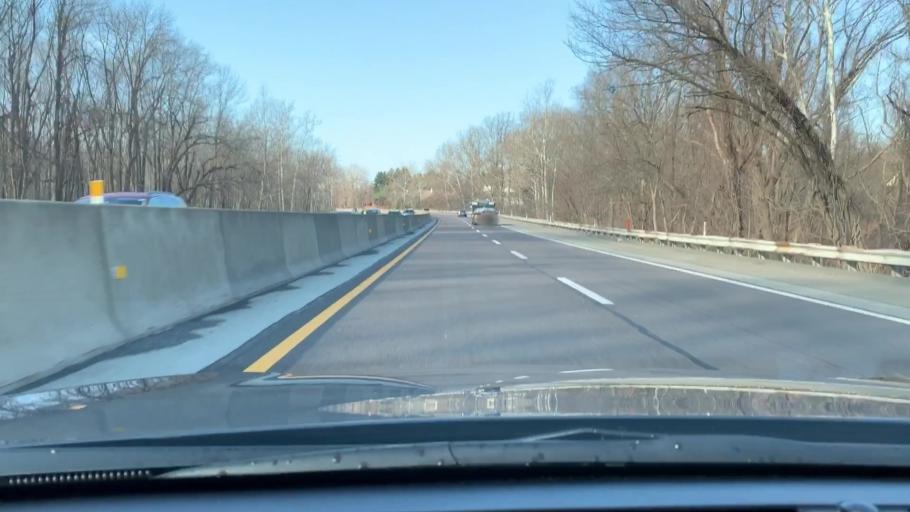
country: US
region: Pennsylvania
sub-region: Chester County
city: Chester Springs
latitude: 40.0635
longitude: -75.6322
